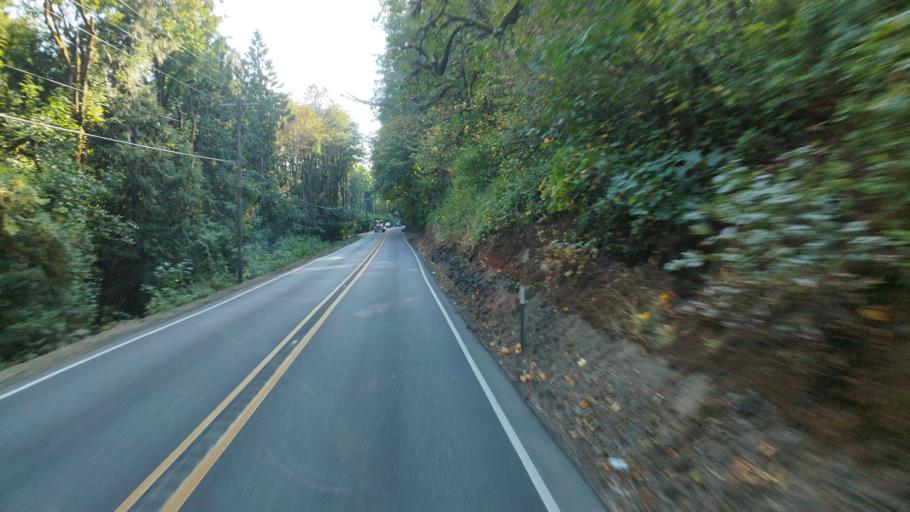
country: US
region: Oregon
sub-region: Washington County
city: Bethany
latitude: 45.6412
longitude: -122.8601
